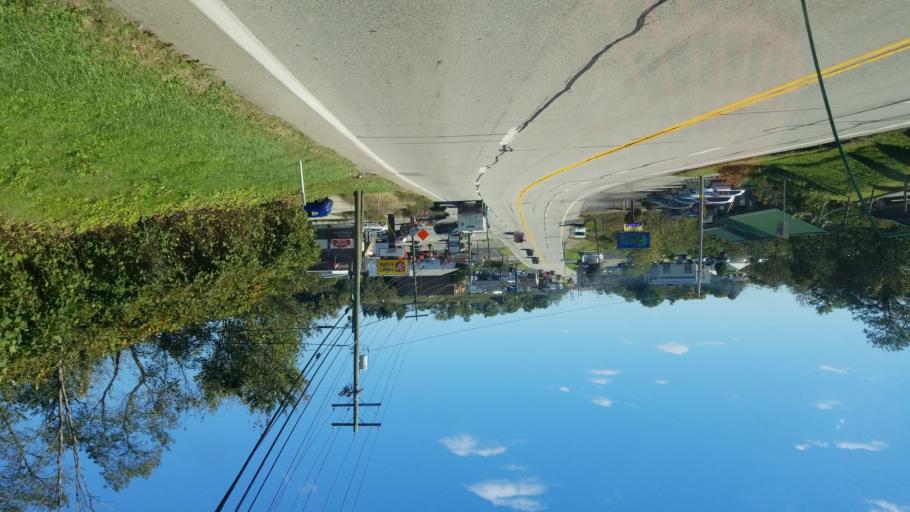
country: US
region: Pennsylvania
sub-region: Westmoreland County
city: Trafford
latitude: 40.3389
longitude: -79.7494
